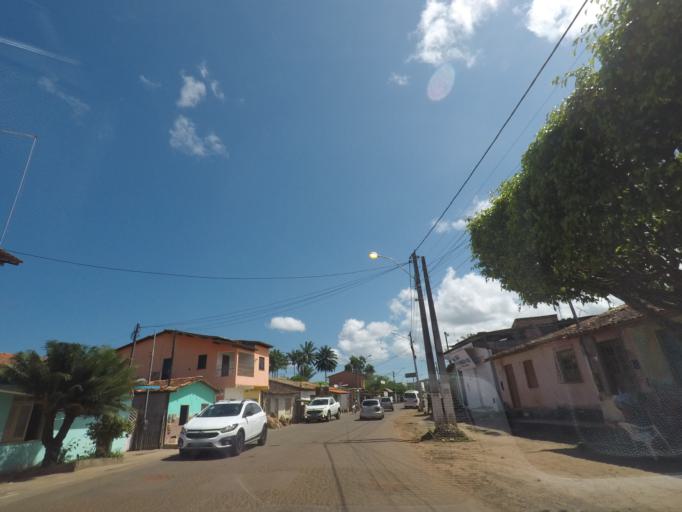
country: BR
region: Bahia
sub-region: Taperoa
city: Taperoa
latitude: -13.5458
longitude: -39.0987
